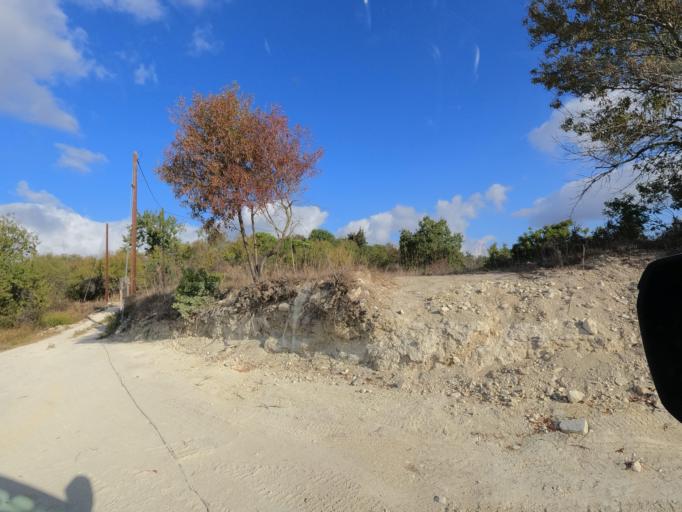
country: CY
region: Pafos
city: Mesogi
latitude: 34.8422
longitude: 32.5031
